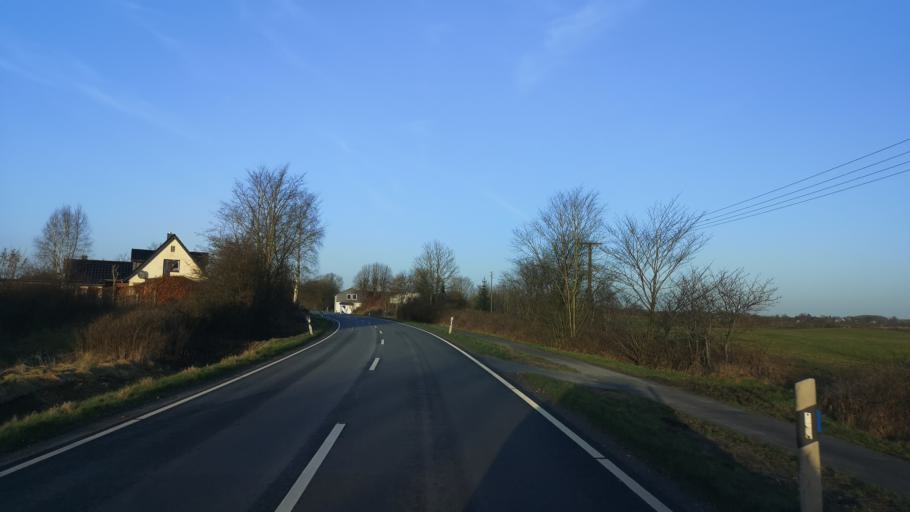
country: DE
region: Schleswig-Holstein
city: Sieverstedt
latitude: 54.6810
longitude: 9.4908
